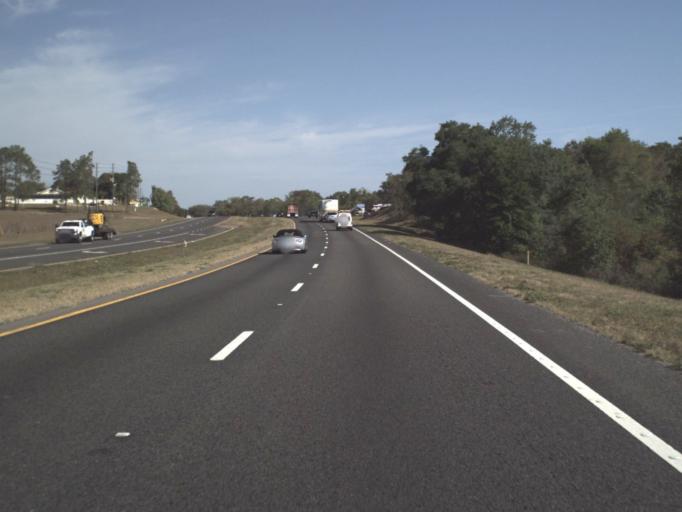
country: US
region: Florida
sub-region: Lake County
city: Hawthorne
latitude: 28.7254
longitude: -81.8628
